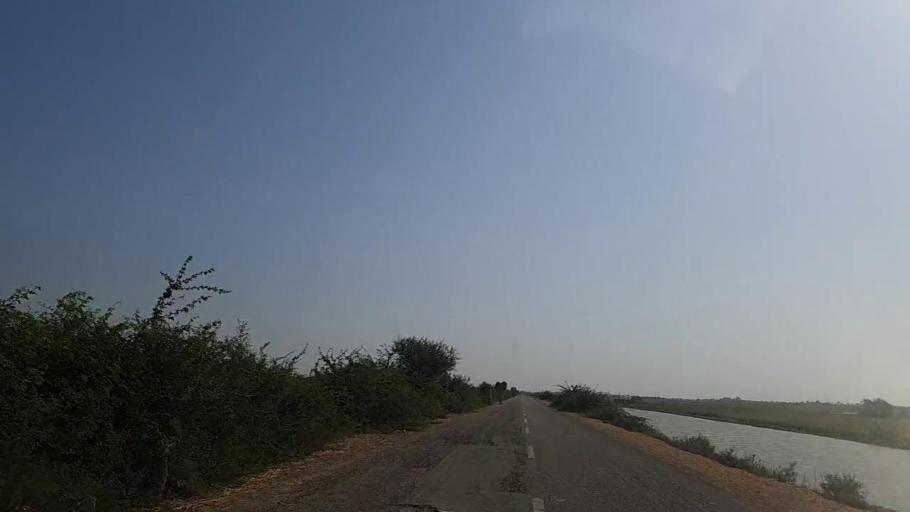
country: PK
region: Sindh
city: Jati
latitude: 24.5036
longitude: 68.2745
